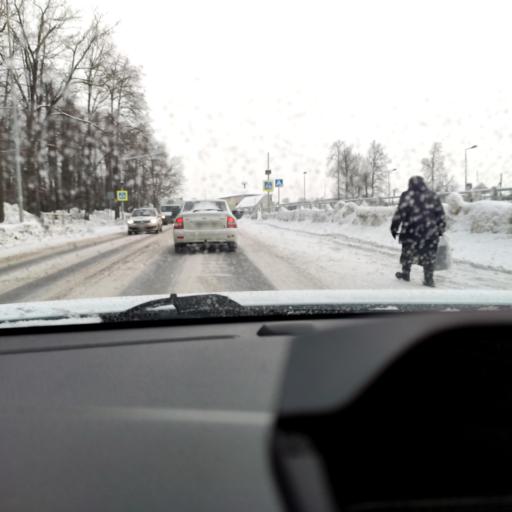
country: RU
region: Tatarstan
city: Vysokaya Gora
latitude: 55.9233
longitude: 49.3052
